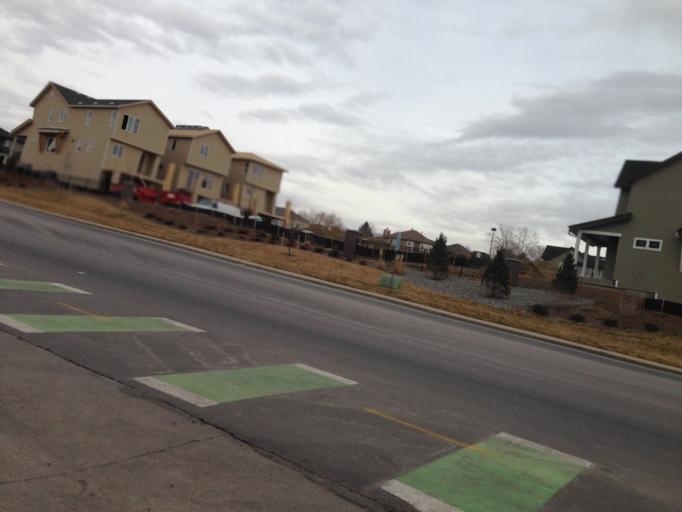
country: US
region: Colorado
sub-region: Adams County
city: Westminster
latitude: 39.8574
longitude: -105.0517
